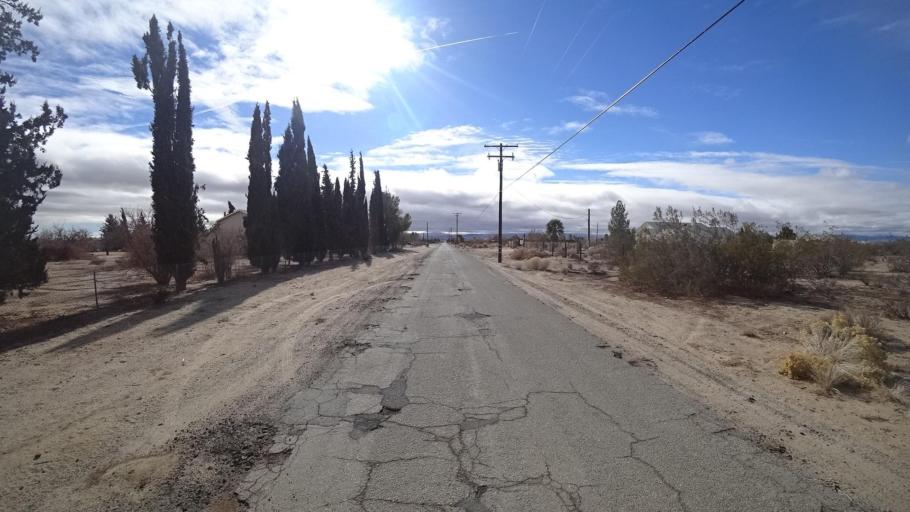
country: US
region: California
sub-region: Kern County
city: Rosamond
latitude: 34.8736
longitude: -118.2202
